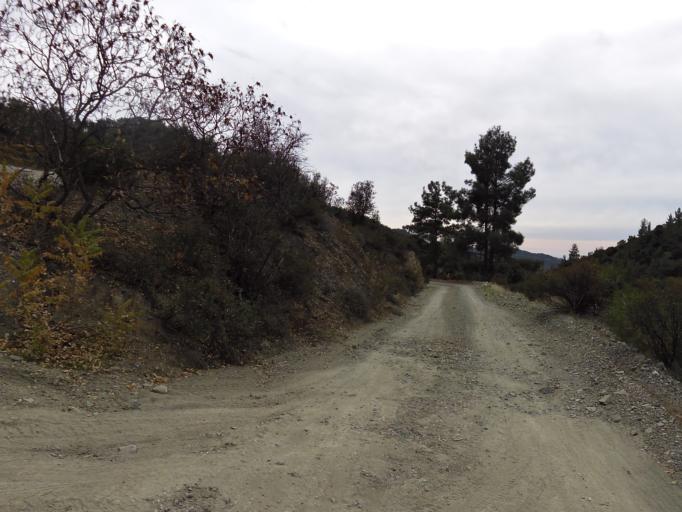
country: CY
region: Limassol
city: Kyperounta
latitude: 34.9233
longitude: 32.9456
